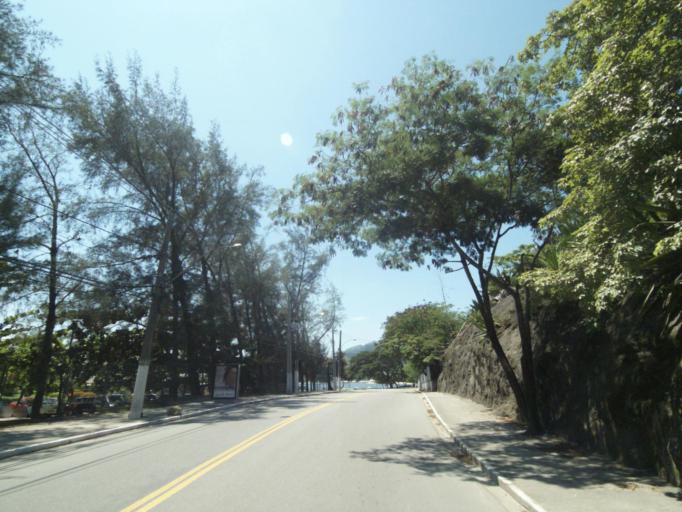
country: BR
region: Rio de Janeiro
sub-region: Niteroi
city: Niteroi
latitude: -22.9368
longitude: -43.1069
